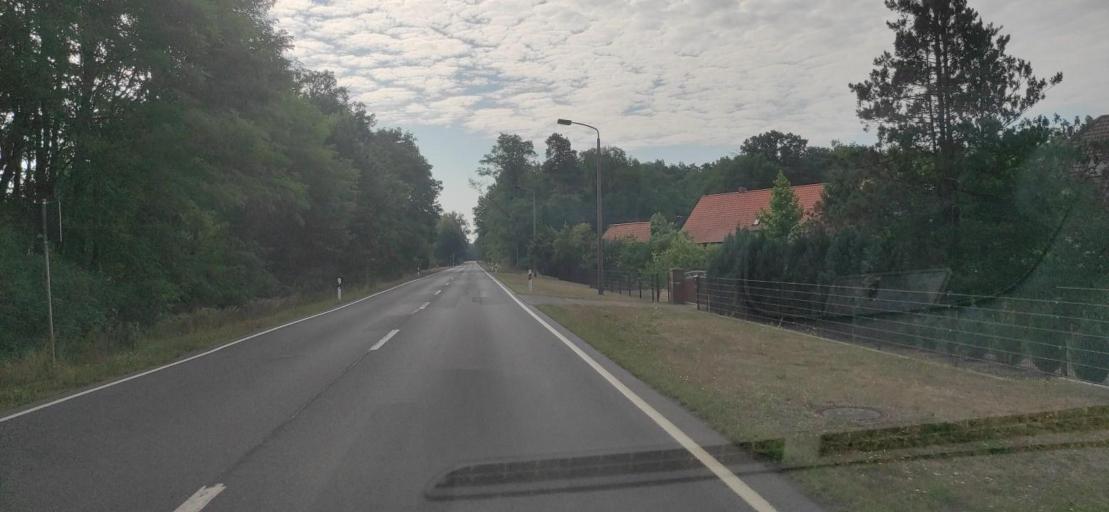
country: DE
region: Brandenburg
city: Forst
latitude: 51.7142
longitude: 14.6679
